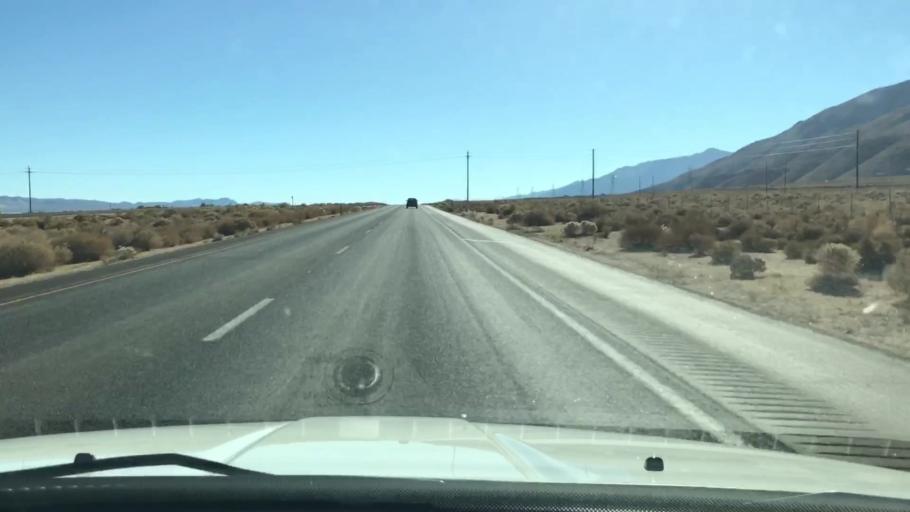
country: US
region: California
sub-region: Inyo County
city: Lone Pine
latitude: 36.4039
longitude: -118.0267
